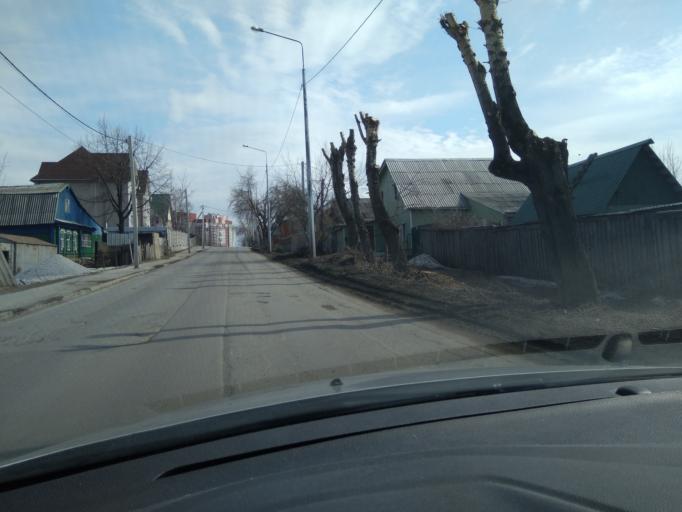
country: RU
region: Sverdlovsk
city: Shuvakish
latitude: 56.8864
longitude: 60.4923
